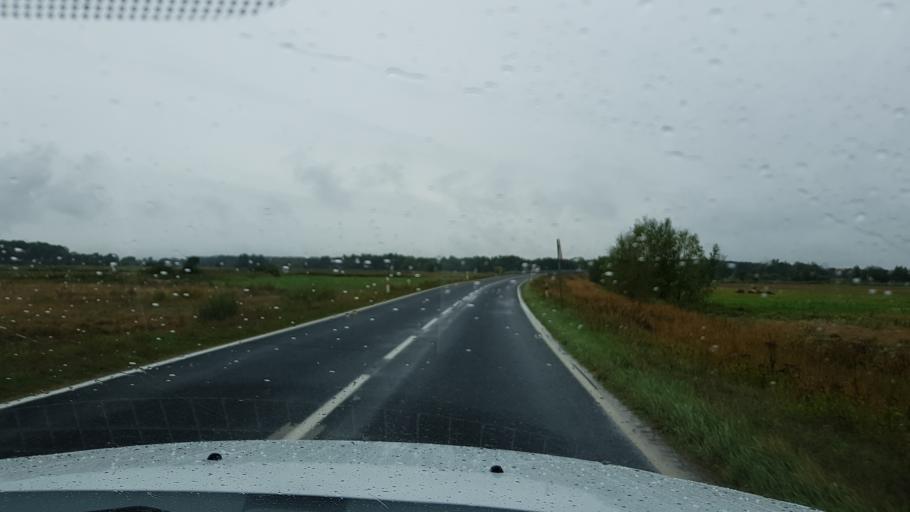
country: PL
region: West Pomeranian Voivodeship
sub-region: Powiat gryfinski
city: Widuchowa
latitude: 53.0645
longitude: 14.3650
